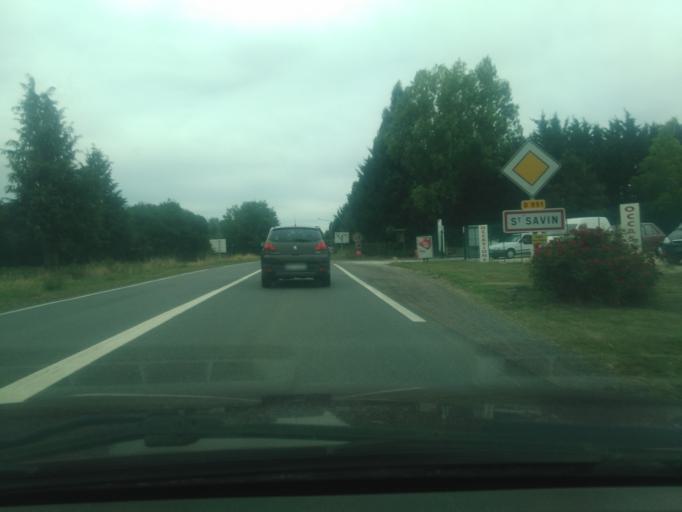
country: FR
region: Poitou-Charentes
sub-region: Departement de la Vienne
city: Saint-Savin
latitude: 46.5628
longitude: 0.8564
